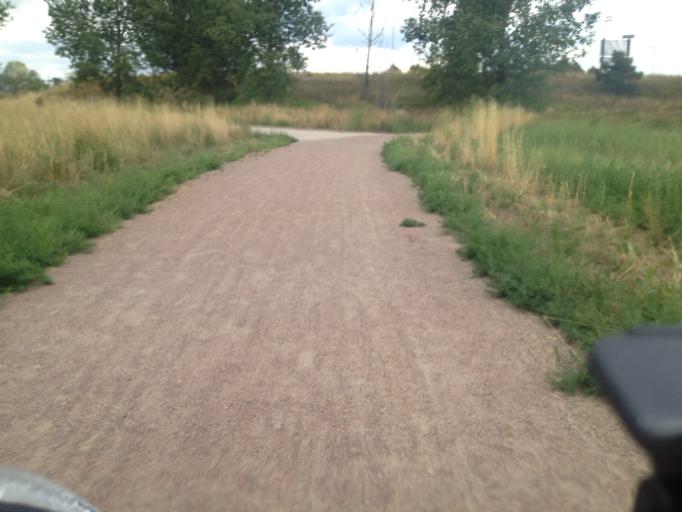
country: US
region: Colorado
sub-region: Boulder County
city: Louisville
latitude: 39.9807
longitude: -105.1235
